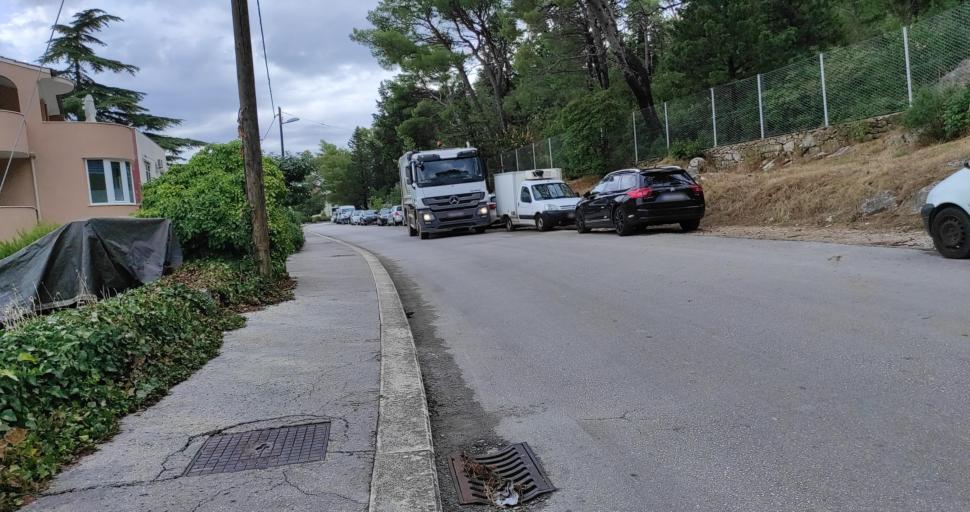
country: HR
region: Splitsko-Dalmatinska
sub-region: Grad Split
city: Split
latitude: 43.5128
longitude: 16.4243
